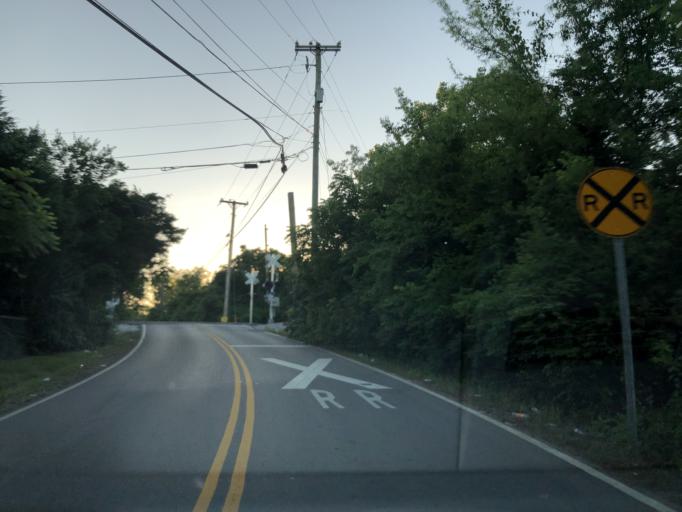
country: US
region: Tennessee
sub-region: Davidson County
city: Goodlettsville
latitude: 36.2881
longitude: -86.7080
